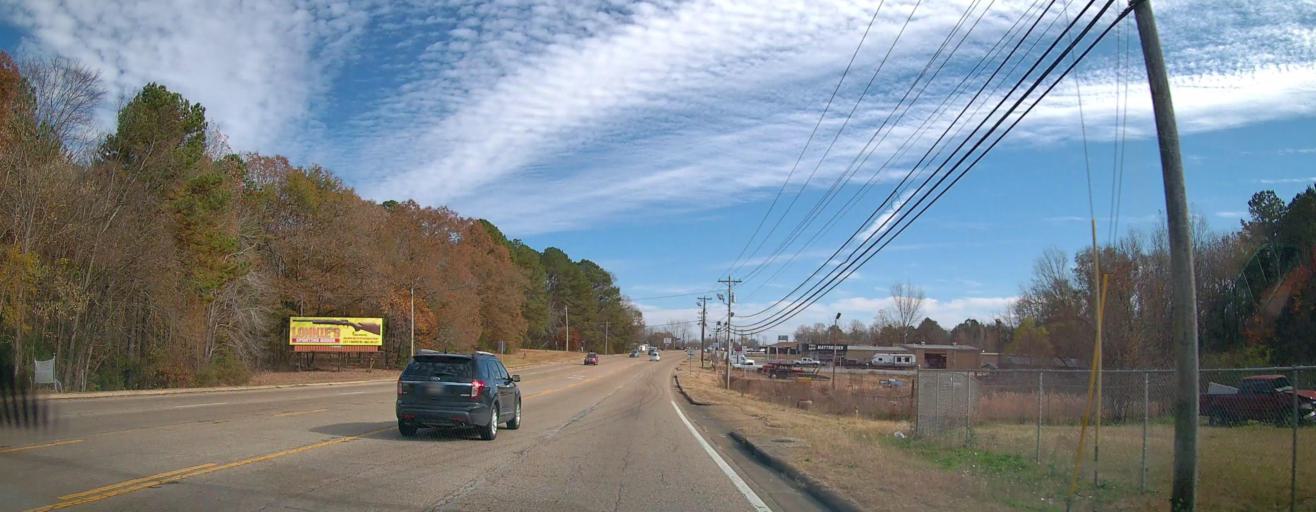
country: US
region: Mississippi
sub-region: Alcorn County
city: Corinth
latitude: 34.9308
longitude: -88.5378
